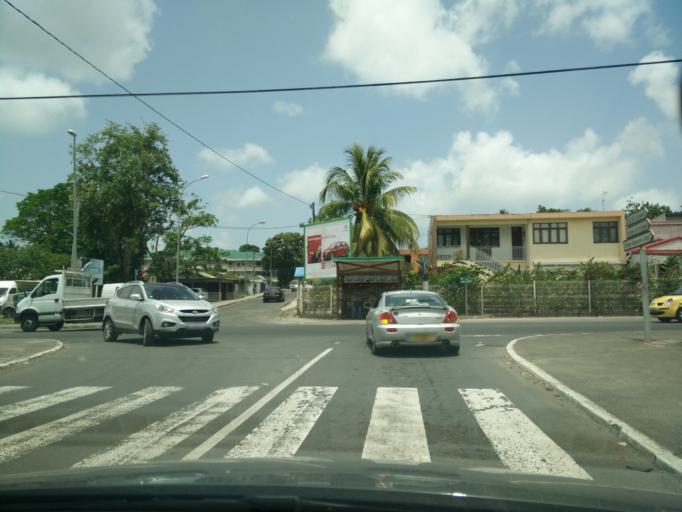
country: GP
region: Guadeloupe
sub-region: Guadeloupe
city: Les Abymes
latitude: 16.2764
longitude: -61.5017
